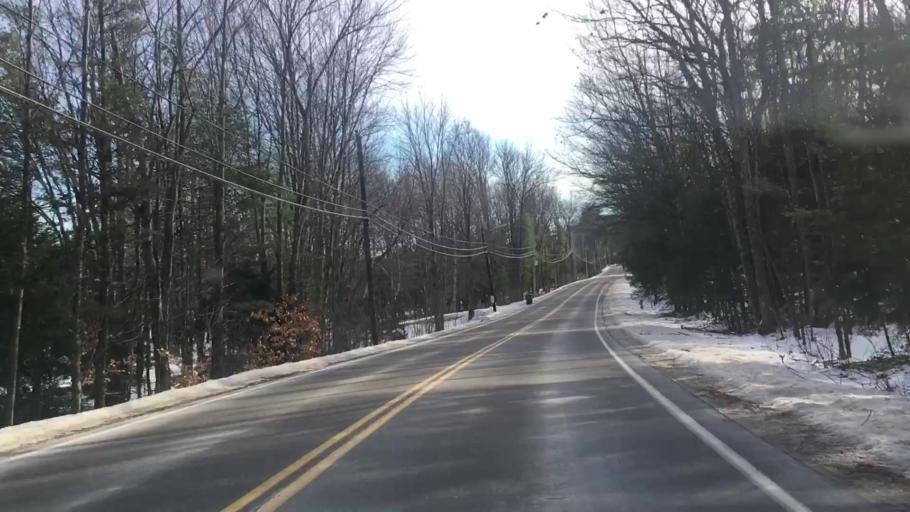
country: US
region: Maine
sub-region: Cumberland County
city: Westbrook
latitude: 43.7028
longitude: -70.3581
